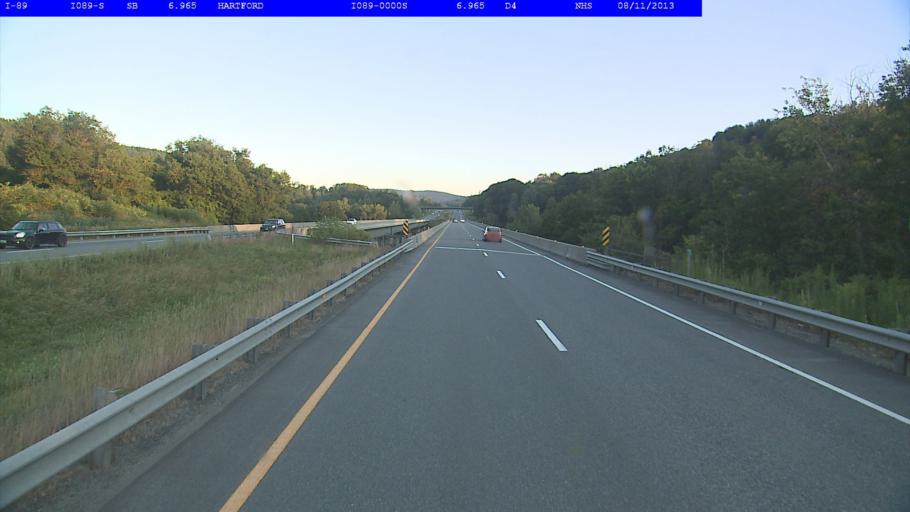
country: US
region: Vermont
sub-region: Windsor County
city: Wilder
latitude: 43.7053
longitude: -72.4128
